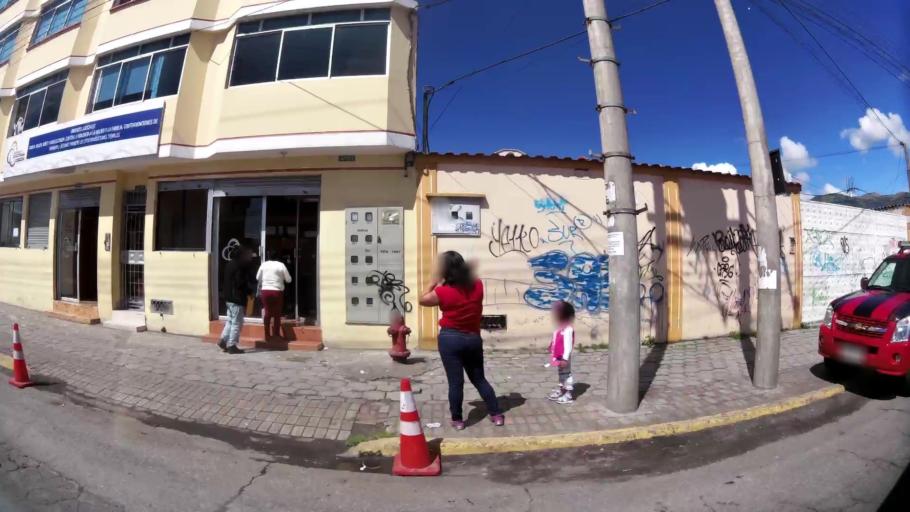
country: EC
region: Pichincha
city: Quito
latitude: -0.2992
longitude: -78.5451
